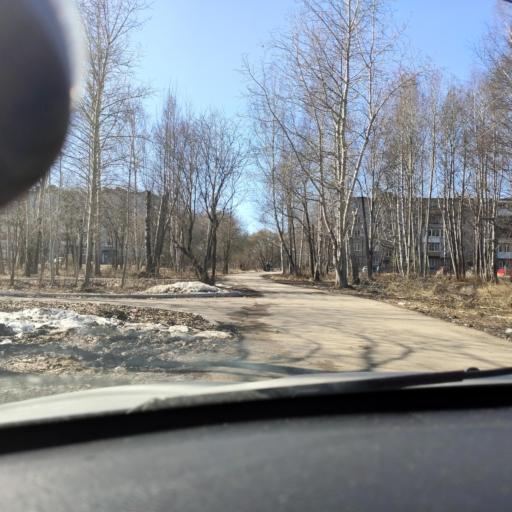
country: RU
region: Perm
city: Polazna
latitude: 58.1471
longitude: 56.4427
